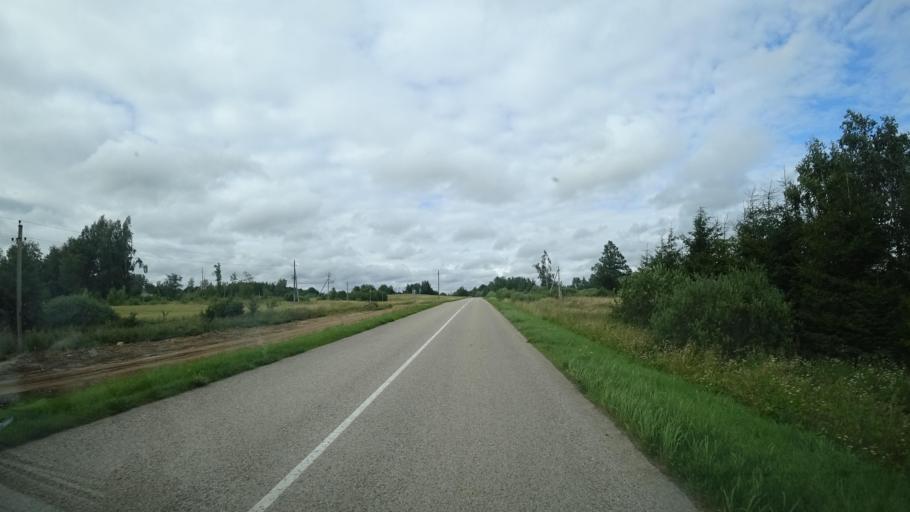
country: LT
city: Virbalis
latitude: 54.4192
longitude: 22.9270
